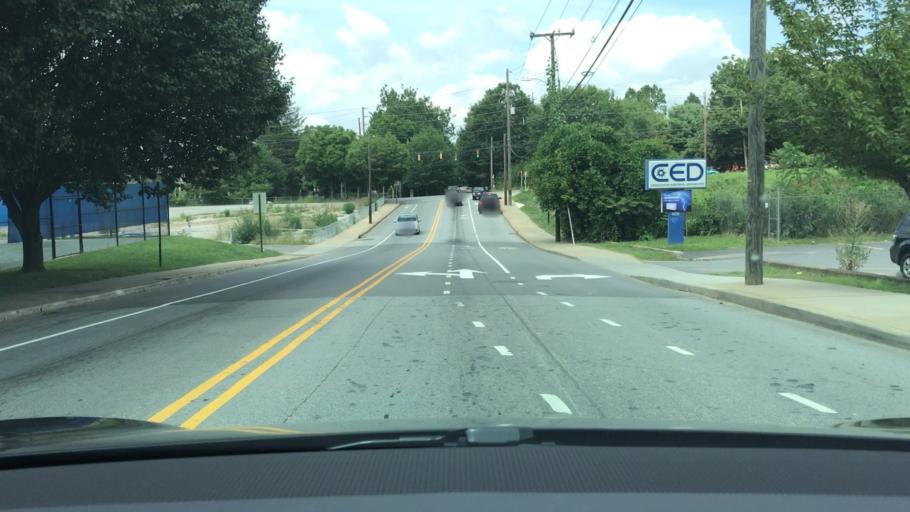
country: US
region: North Carolina
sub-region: Buncombe County
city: Asheville
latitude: 35.5912
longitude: -82.5608
